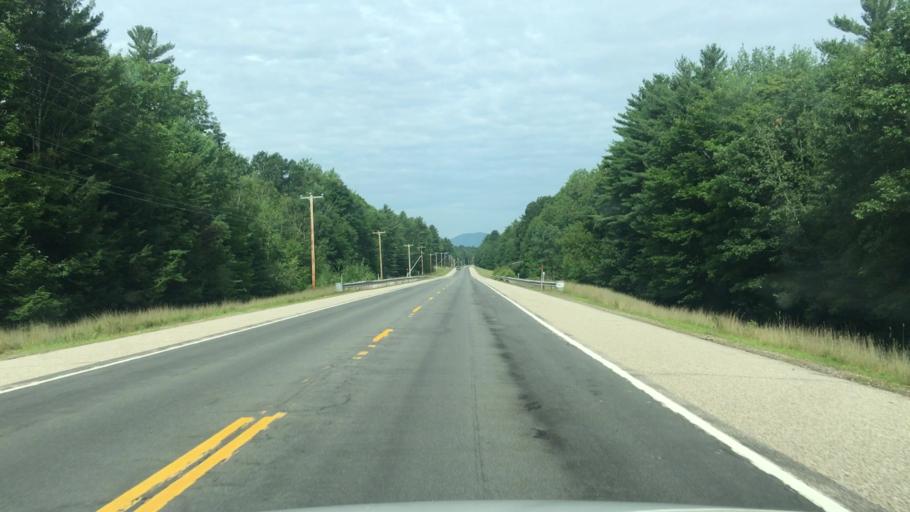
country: US
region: New Hampshire
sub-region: Carroll County
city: Tamworth
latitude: 43.8248
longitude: -71.2337
